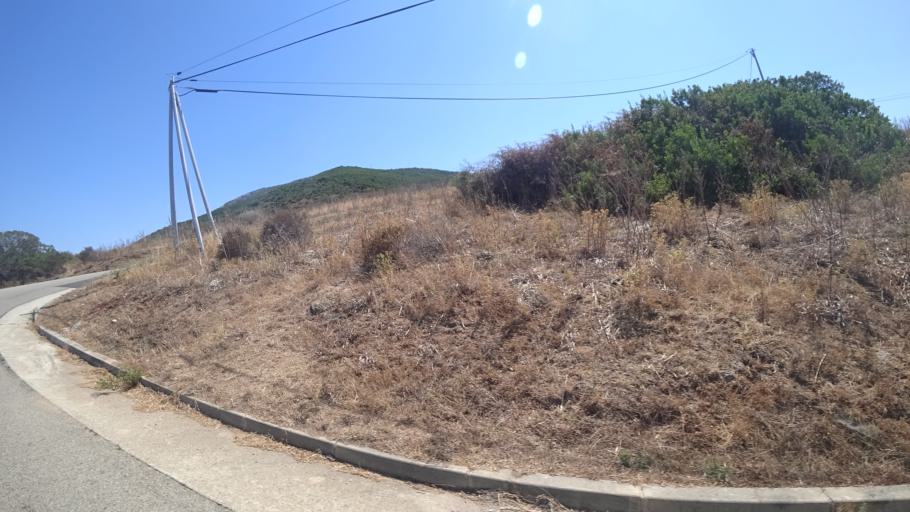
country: FR
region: Corsica
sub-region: Departement de la Corse-du-Sud
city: Alata
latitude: 41.9742
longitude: 8.6894
